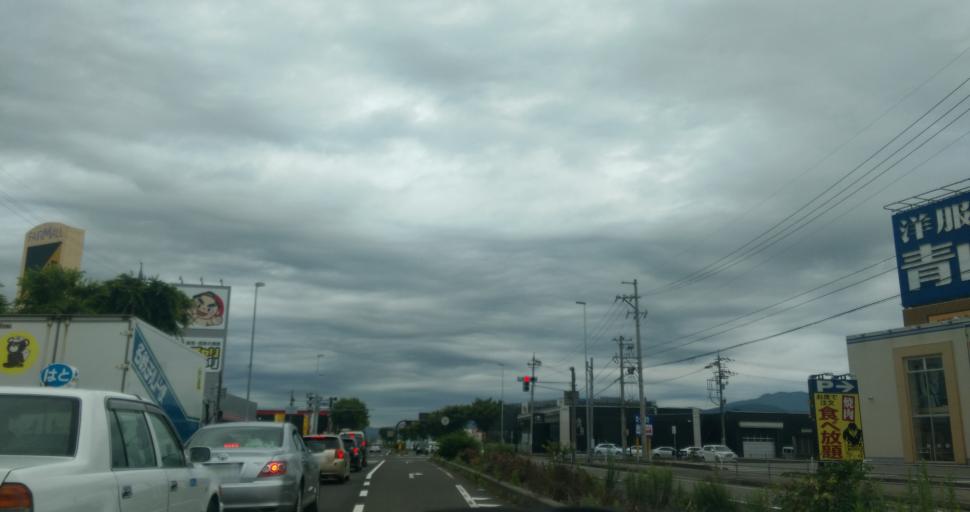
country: JP
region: Fukui
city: Fukui-shi
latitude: 36.0971
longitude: 136.2523
